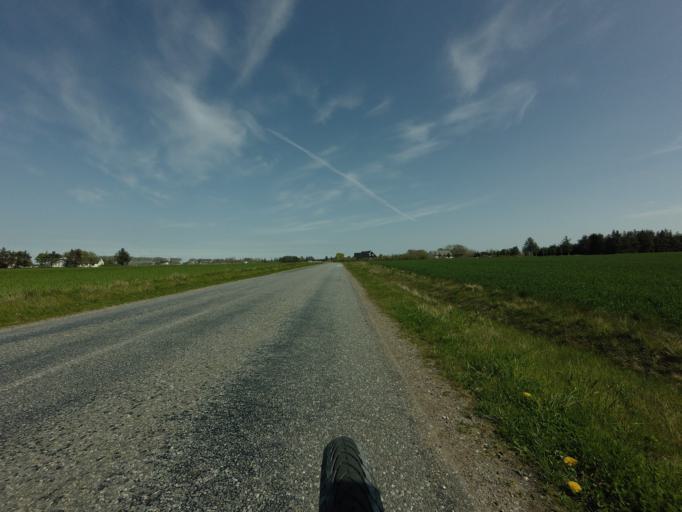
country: DK
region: North Denmark
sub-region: Jammerbugt Kommune
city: Pandrup
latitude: 57.2254
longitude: 9.6531
